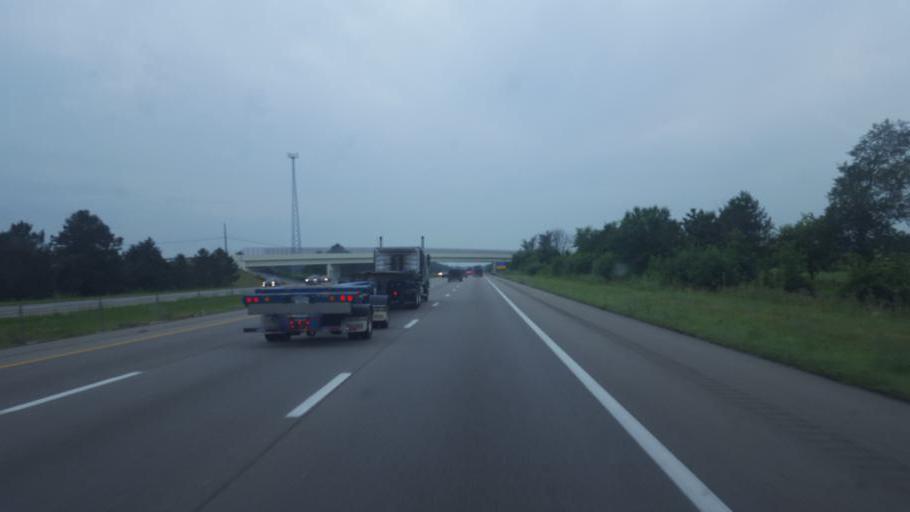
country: US
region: Ohio
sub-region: Delaware County
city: Sunbury
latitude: 40.3405
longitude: -82.8769
